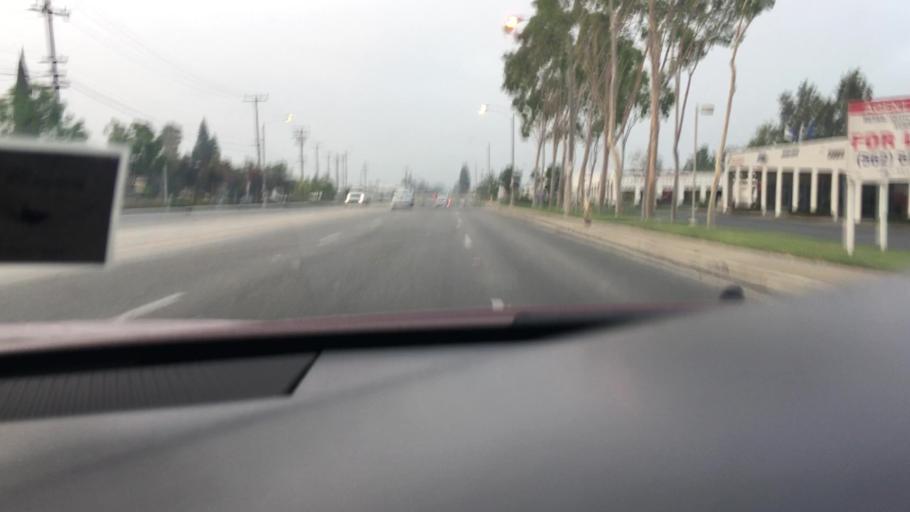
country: US
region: California
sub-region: Los Angeles County
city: La Mirada
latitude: 33.9011
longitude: -118.0292
